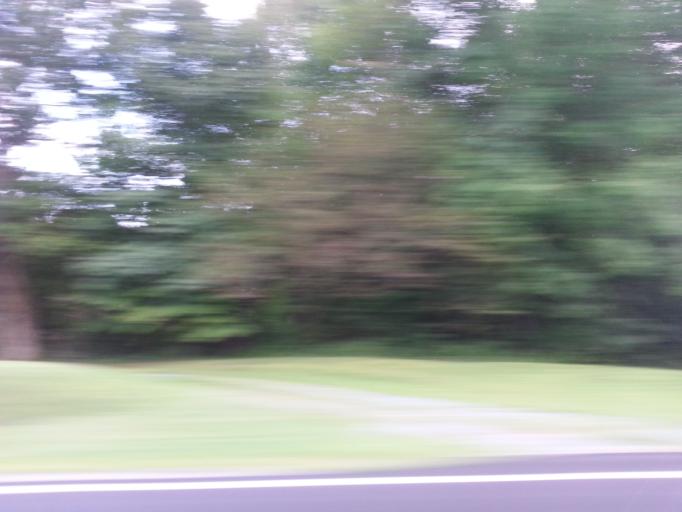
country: US
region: Tennessee
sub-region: Carter County
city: Hunter
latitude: 36.4632
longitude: -82.0096
